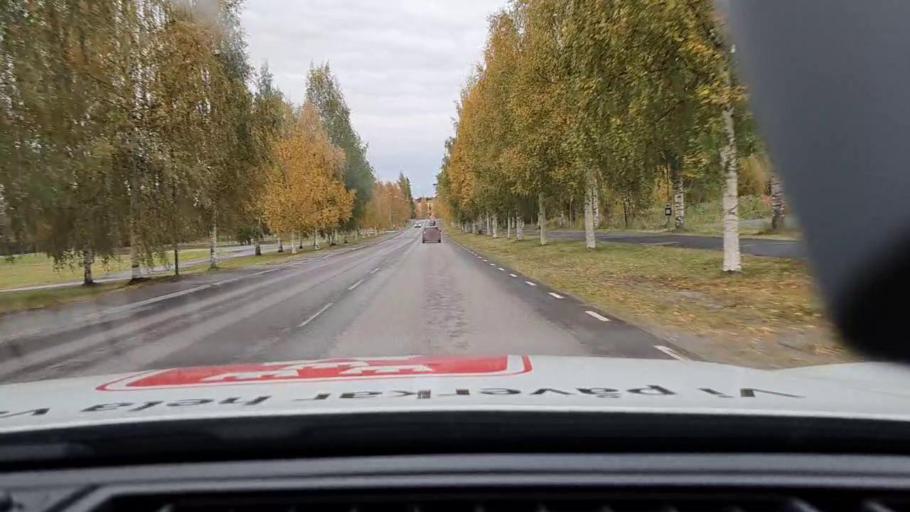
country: SE
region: Norrbotten
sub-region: Bodens Kommun
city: Boden
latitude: 65.8169
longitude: 21.6692
